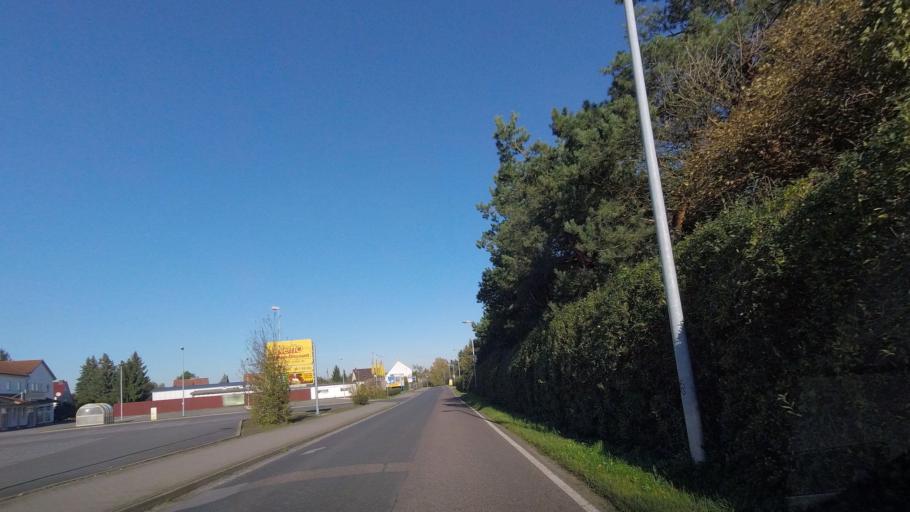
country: DE
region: Saxony-Anhalt
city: Zahna
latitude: 51.9131
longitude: 12.7805
